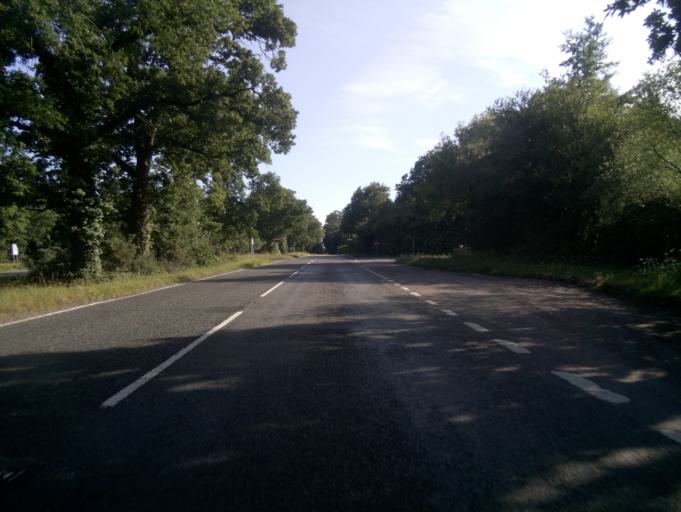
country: GB
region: England
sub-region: Hampshire
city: Romsey
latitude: 50.9661
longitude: -1.5236
